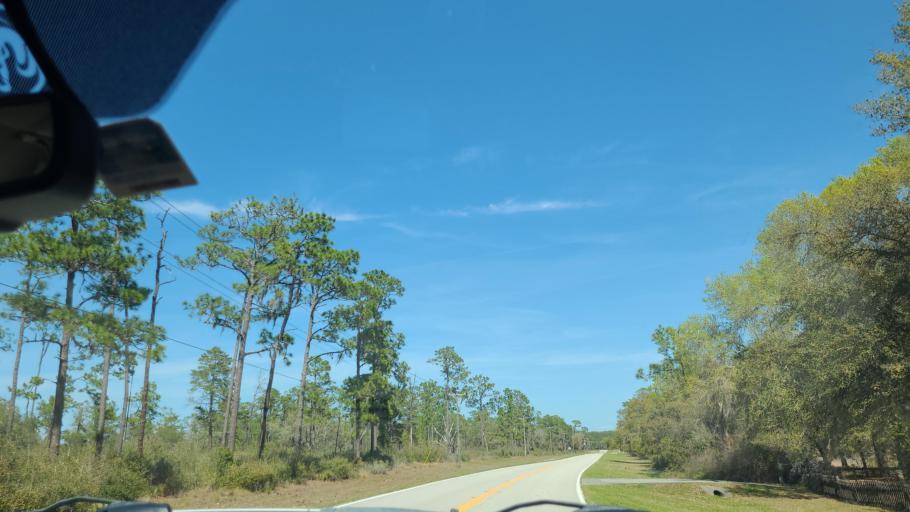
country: US
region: Florida
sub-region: Putnam County
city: Interlachen
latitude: 29.3731
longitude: -81.8021
